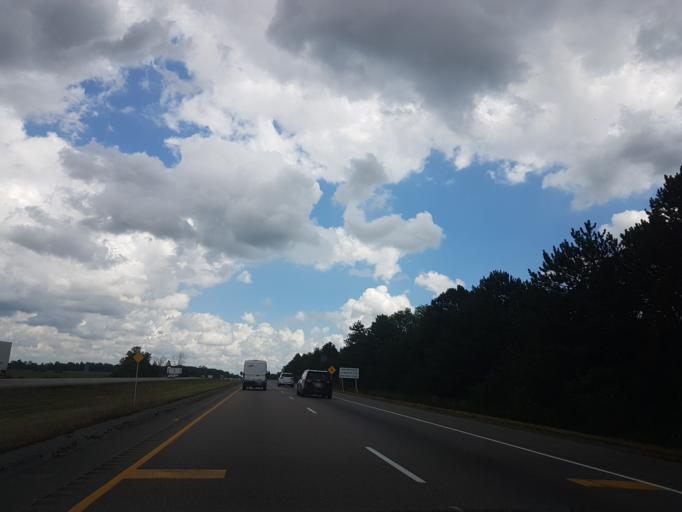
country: CA
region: Ontario
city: Deseronto
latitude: 44.2390
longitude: -77.1023
